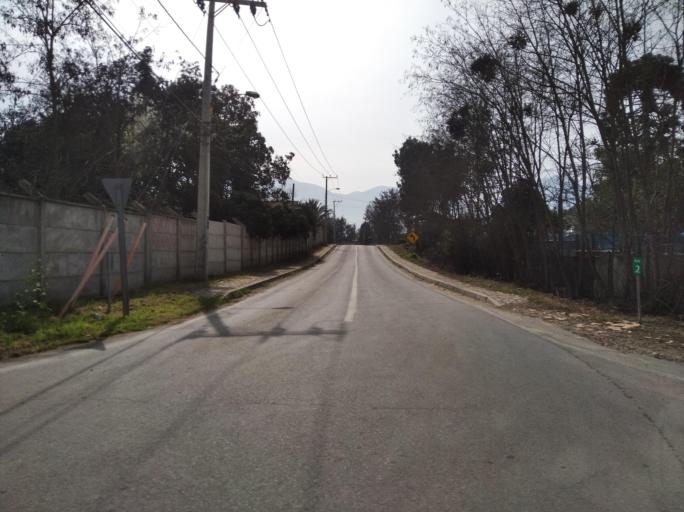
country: CL
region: Valparaiso
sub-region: Provincia de Marga Marga
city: Limache
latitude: -33.0057
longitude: -71.2246
